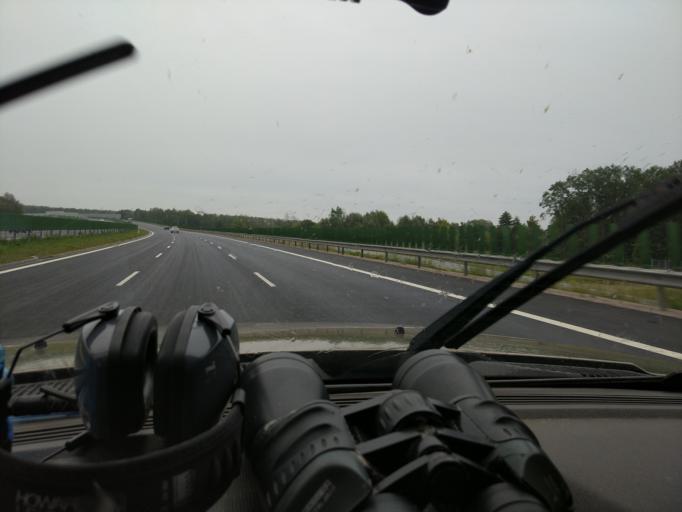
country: PL
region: Masovian Voivodeship
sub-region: Powiat wolominski
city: Kobylka
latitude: 52.3555
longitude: 21.1784
